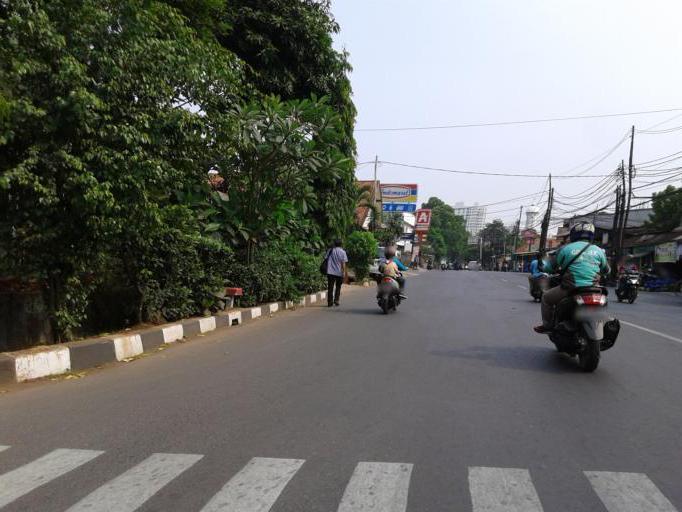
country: ID
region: West Java
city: Pamulang
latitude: -6.3106
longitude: 106.7811
